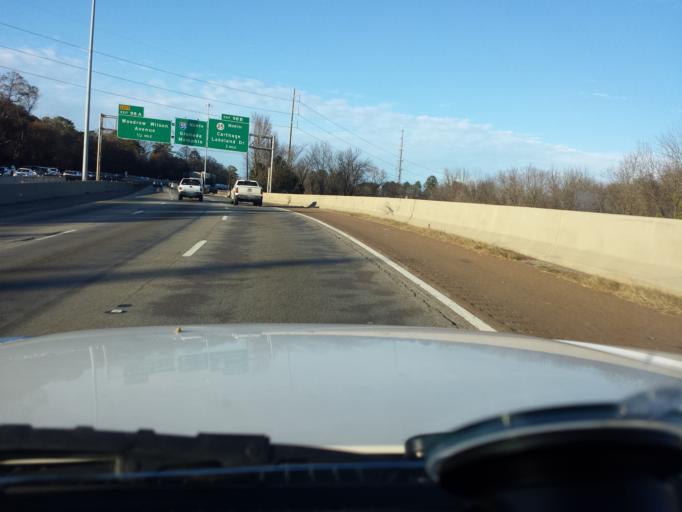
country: US
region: Mississippi
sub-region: Rankin County
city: Flowood
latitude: 32.3169
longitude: -90.1580
